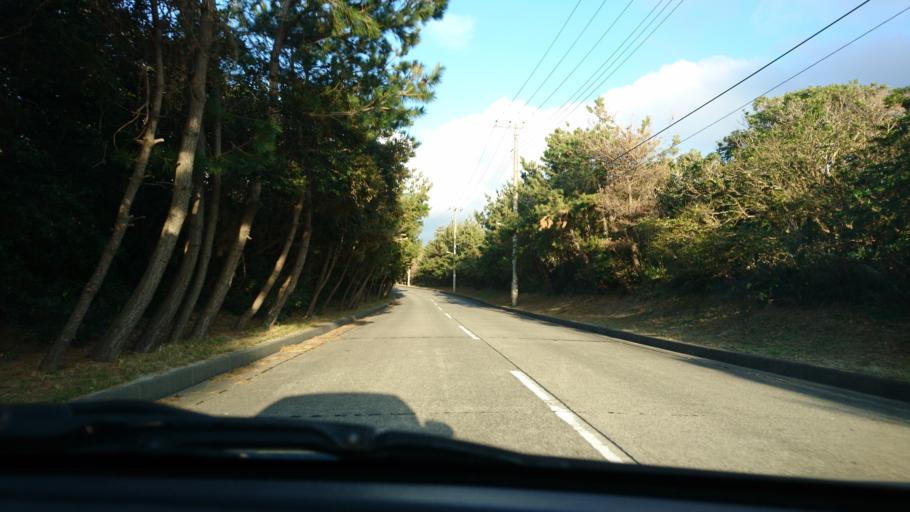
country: JP
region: Shizuoka
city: Shimoda
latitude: 34.3614
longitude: 139.2483
